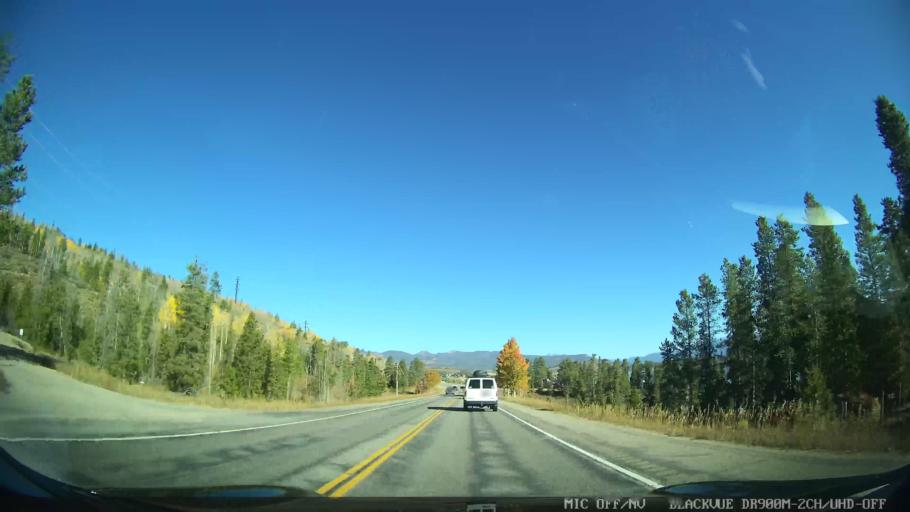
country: US
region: Colorado
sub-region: Grand County
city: Granby
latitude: 40.1544
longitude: -105.8894
